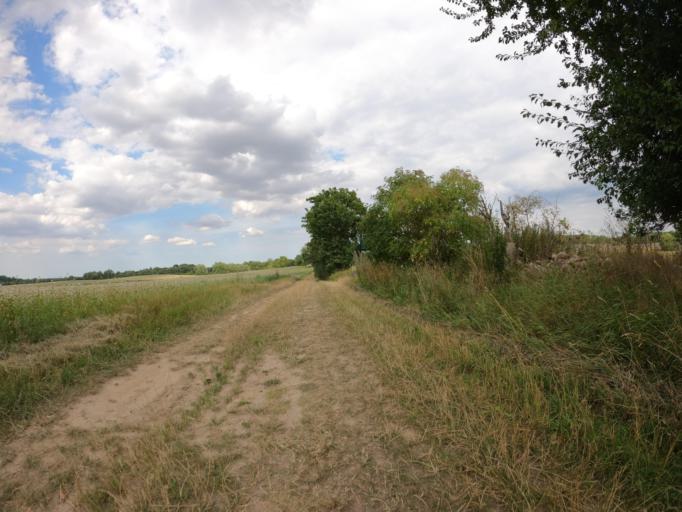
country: DE
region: Mecklenburg-Vorpommern
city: Woldegk
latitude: 53.4007
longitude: 13.6144
